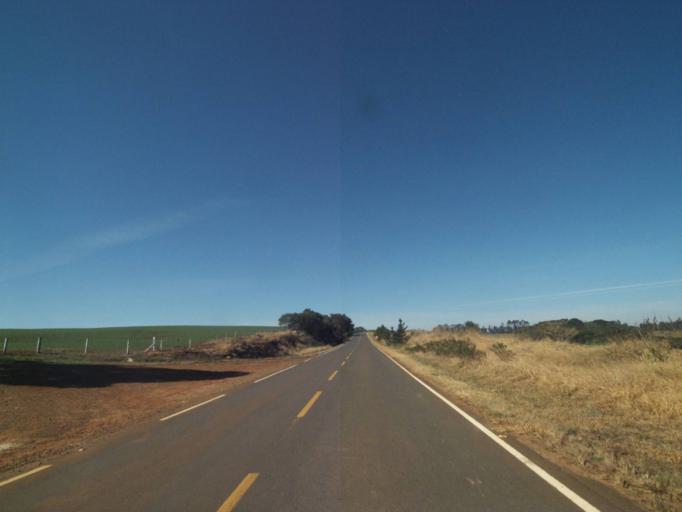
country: BR
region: Parana
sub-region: Tibagi
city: Tibagi
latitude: -24.4898
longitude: -50.4683
